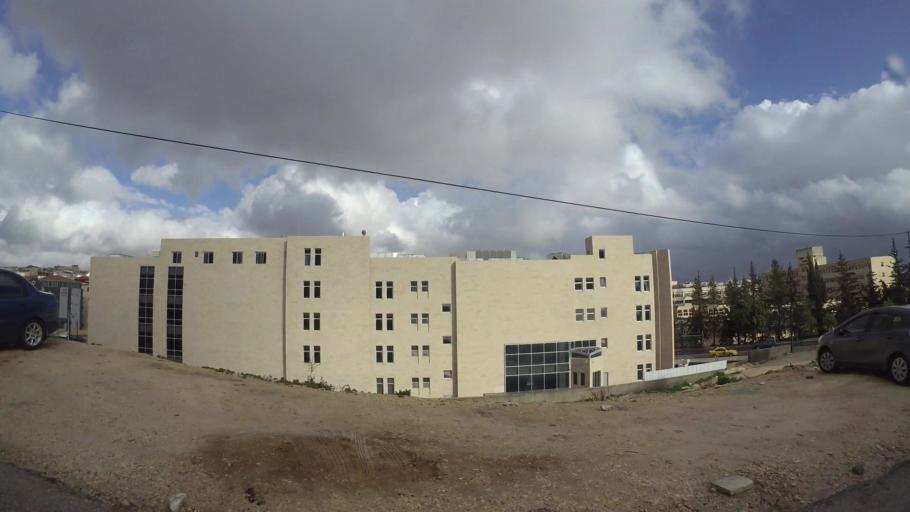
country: JO
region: Amman
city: Al Jubayhah
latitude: 32.0215
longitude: 35.8702
